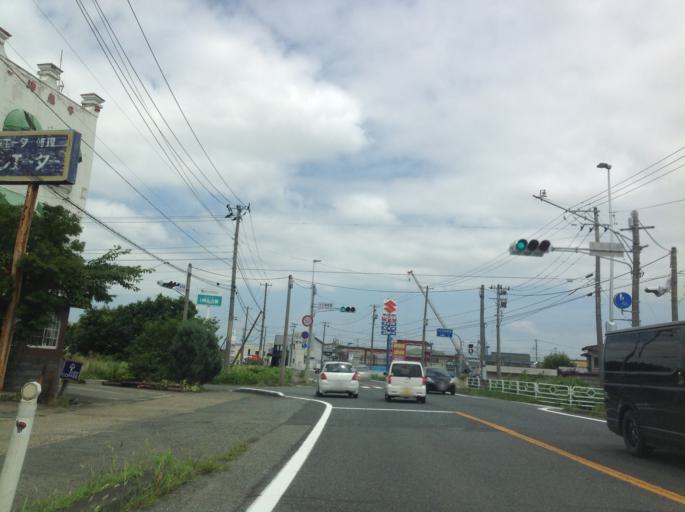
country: JP
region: Iwate
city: Mizusawa
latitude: 39.1304
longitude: 141.1495
